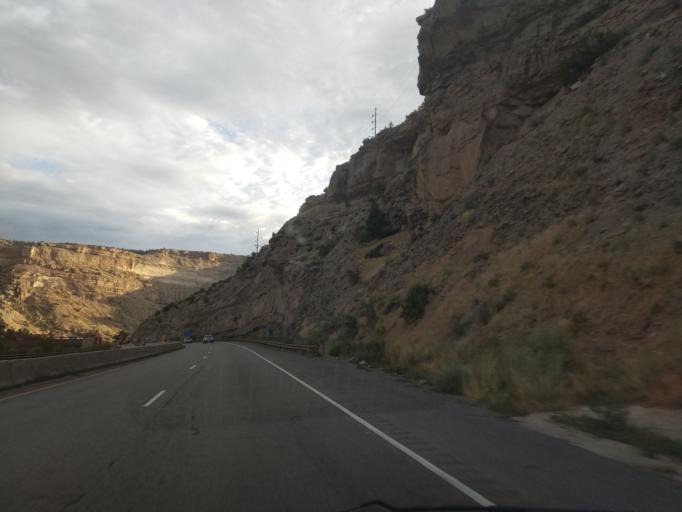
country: US
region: Colorado
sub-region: Mesa County
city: Palisade
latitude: 39.1876
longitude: -108.2804
